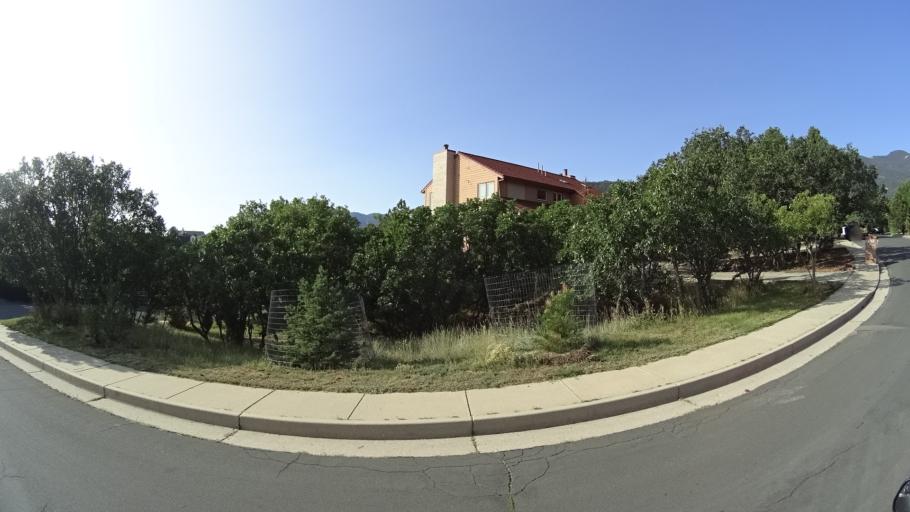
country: US
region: Colorado
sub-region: El Paso County
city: Colorado Springs
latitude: 38.8242
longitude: -104.8738
